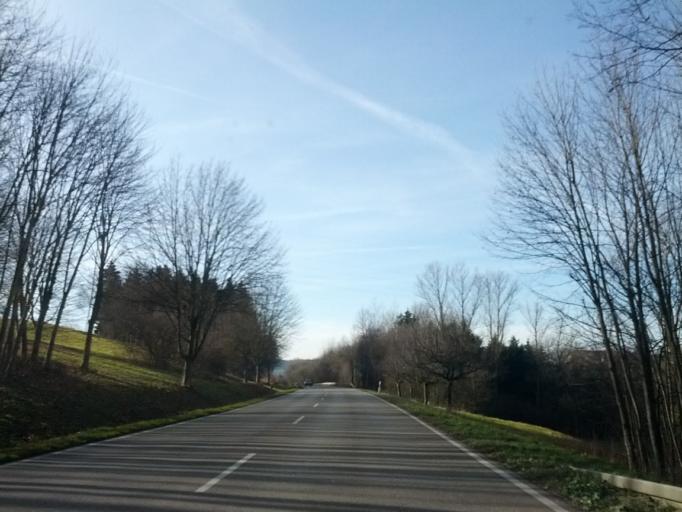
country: DE
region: Baden-Wuerttemberg
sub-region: Regierungsbezirk Stuttgart
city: Ellwangen
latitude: 48.9629
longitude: 10.1539
